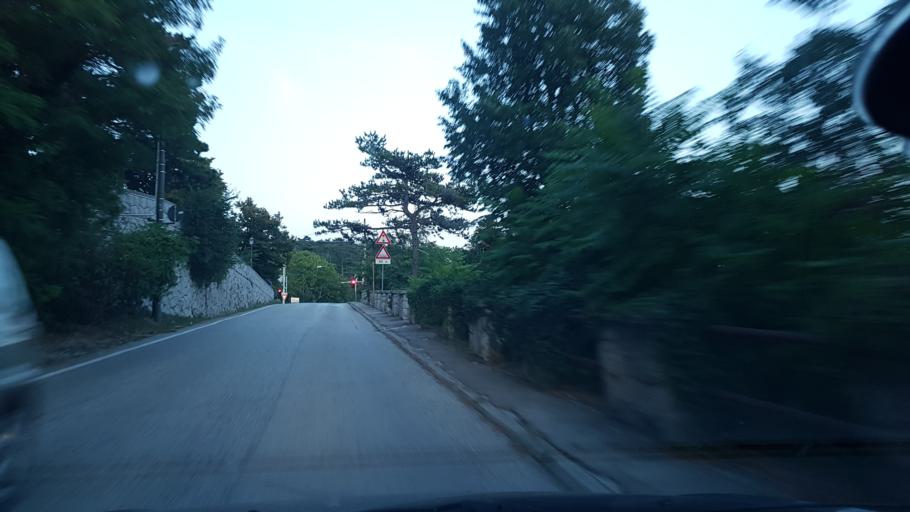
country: IT
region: Friuli Venezia Giulia
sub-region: Provincia di Trieste
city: Villa Opicina
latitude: 45.6795
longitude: 13.7800
